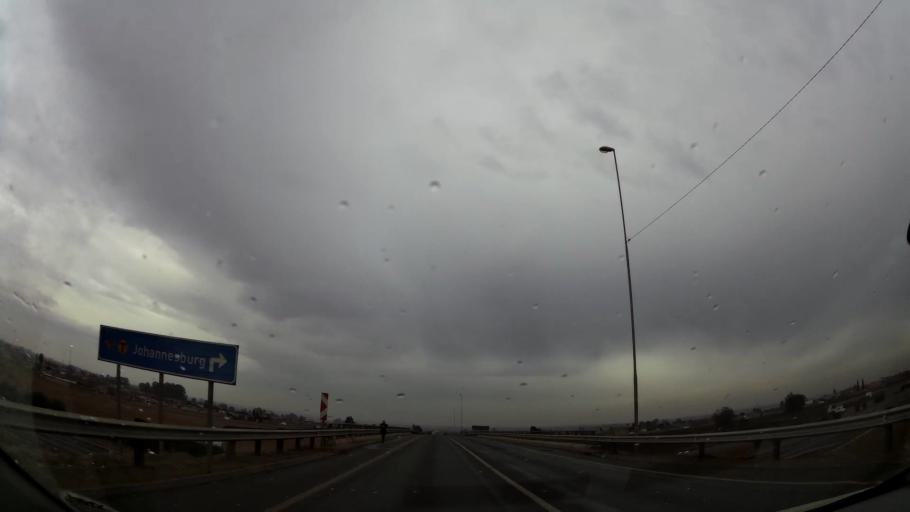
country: ZA
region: Gauteng
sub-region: Ekurhuleni Metropolitan Municipality
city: Germiston
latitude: -26.3200
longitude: 28.1915
